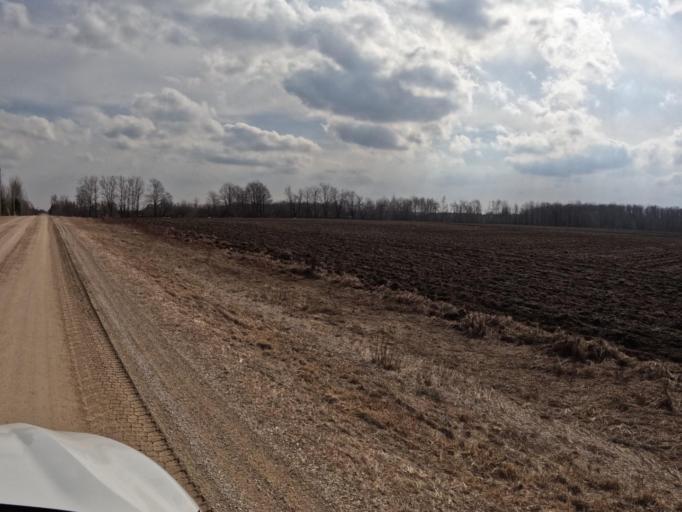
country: CA
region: Ontario
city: Shelburne
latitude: 43.9403
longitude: -80.3107
